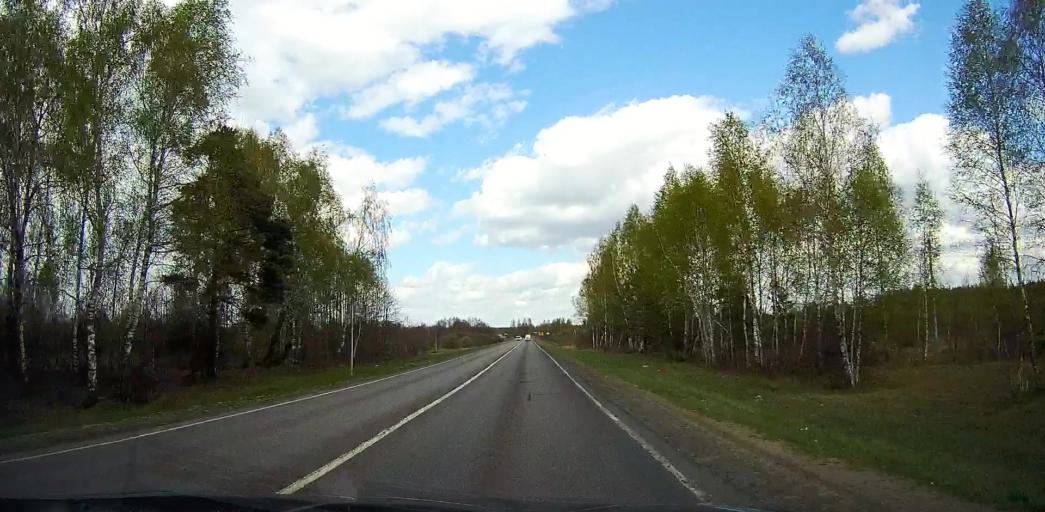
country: RU
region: Moskovskaya
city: Davydovo
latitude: 55.6303
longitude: 38.8645
